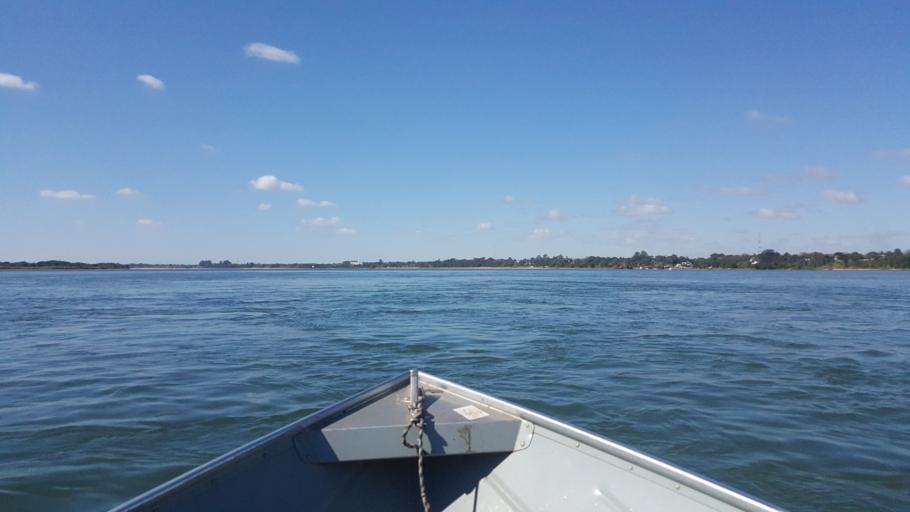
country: AR
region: Corrientes
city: Ituzaingo
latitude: -27.5839
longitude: -56.7089
